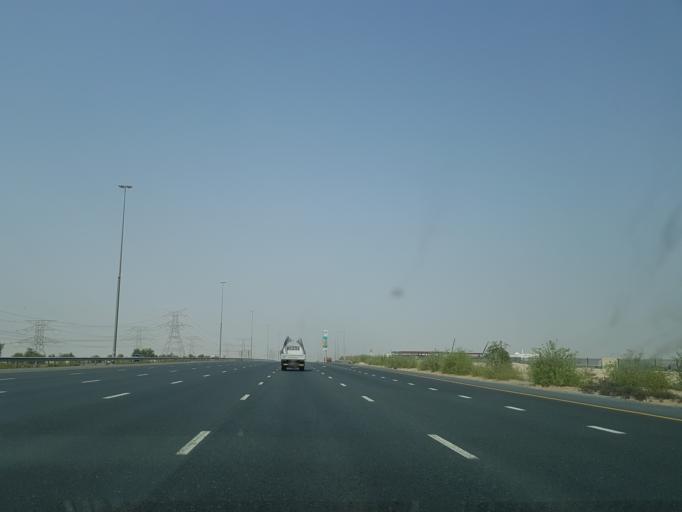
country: AE
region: Dubai
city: Dubai
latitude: 25.0717
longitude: 55.3644
